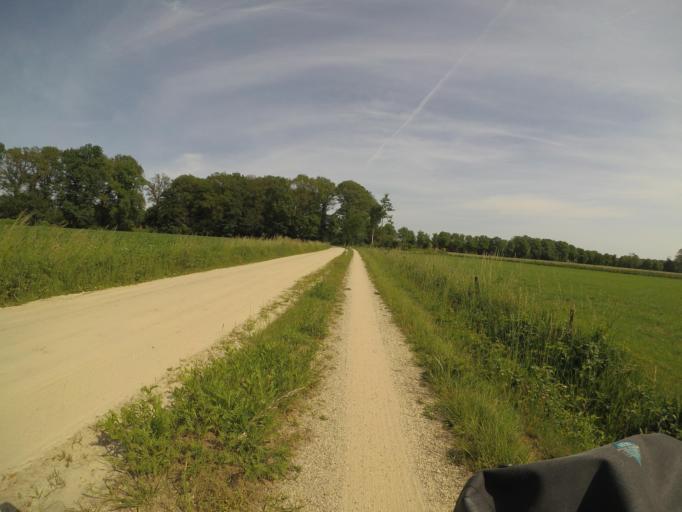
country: NL
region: Gelderland
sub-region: Gemeente Winterswijk
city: Winterswijk
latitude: 51.9316
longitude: 6.6942
